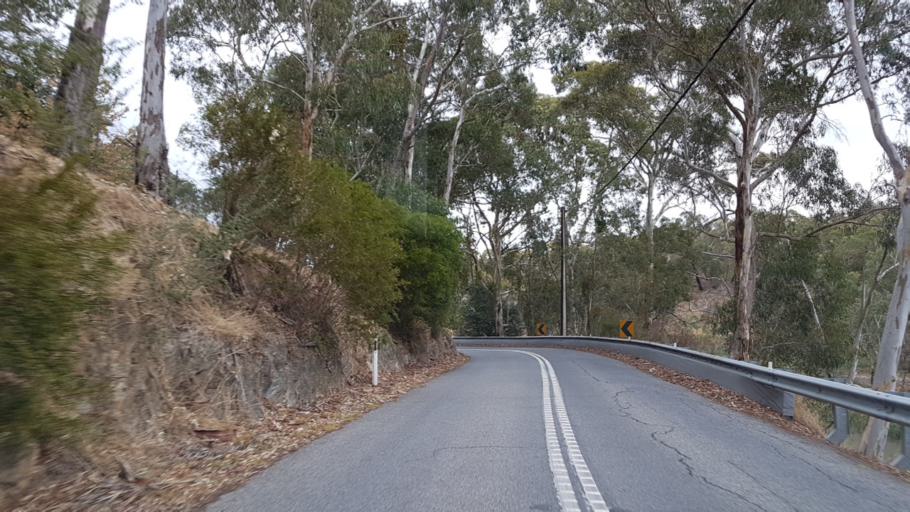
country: AU
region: South Australia
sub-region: Adelaide Hills
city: Gumeracha
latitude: -34.8399
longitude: 138.8143
